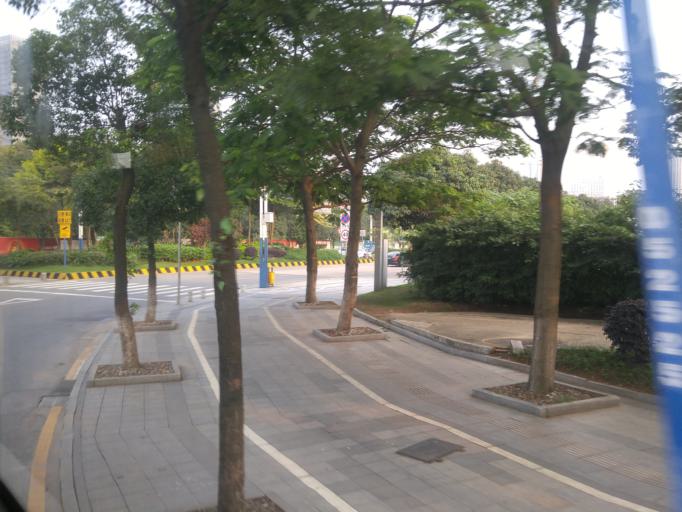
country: CN
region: Guangdong
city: Foshan
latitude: 23.0697
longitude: 113.1401
